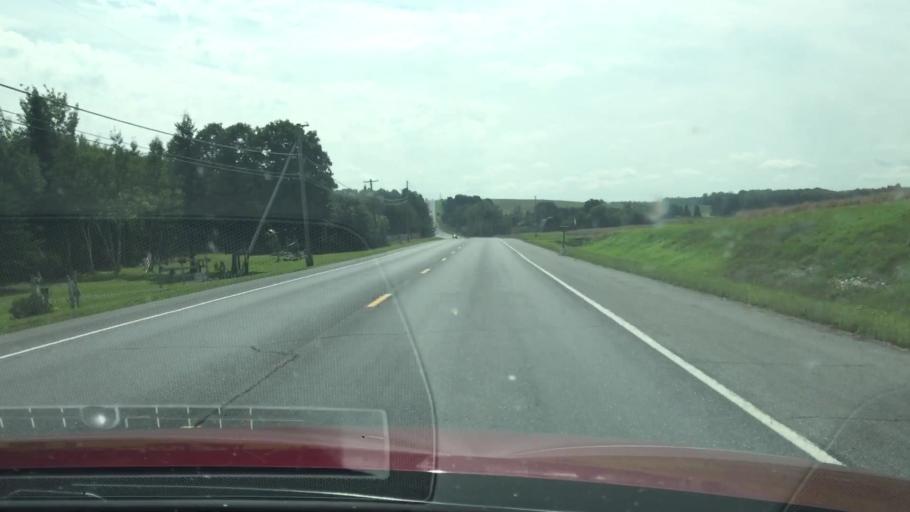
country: US
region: Maine
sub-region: Aroostook County
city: Easton
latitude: 46.5876
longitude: -67.9614
